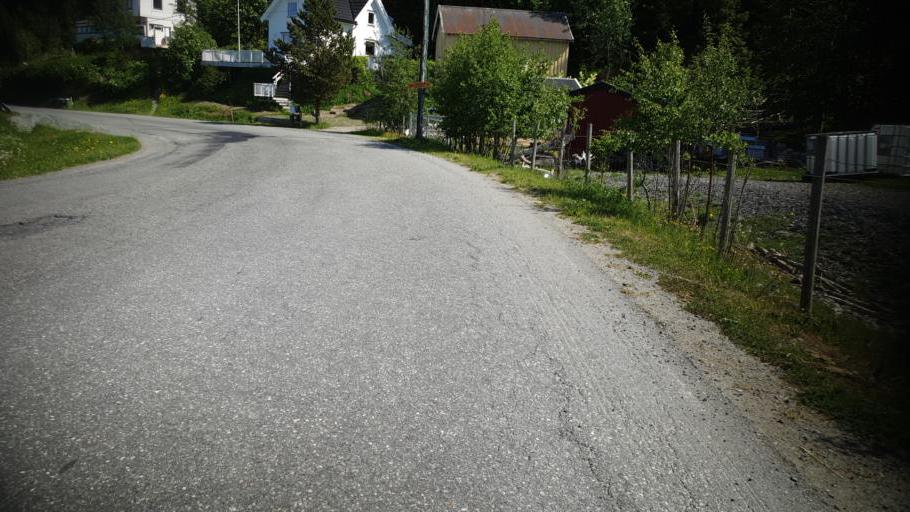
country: NO
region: Sor-Trondelag
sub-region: Malvik
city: Malvik
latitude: 63.4320
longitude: 10.5963
